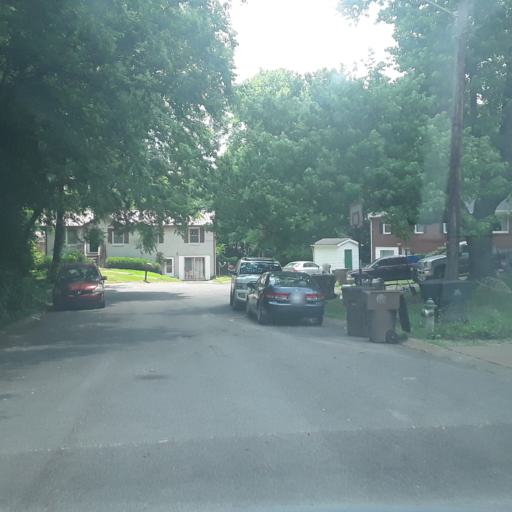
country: US
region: Tennessee
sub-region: Williamson County
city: Brentwood Estates
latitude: 36.0539
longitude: -86.6986
